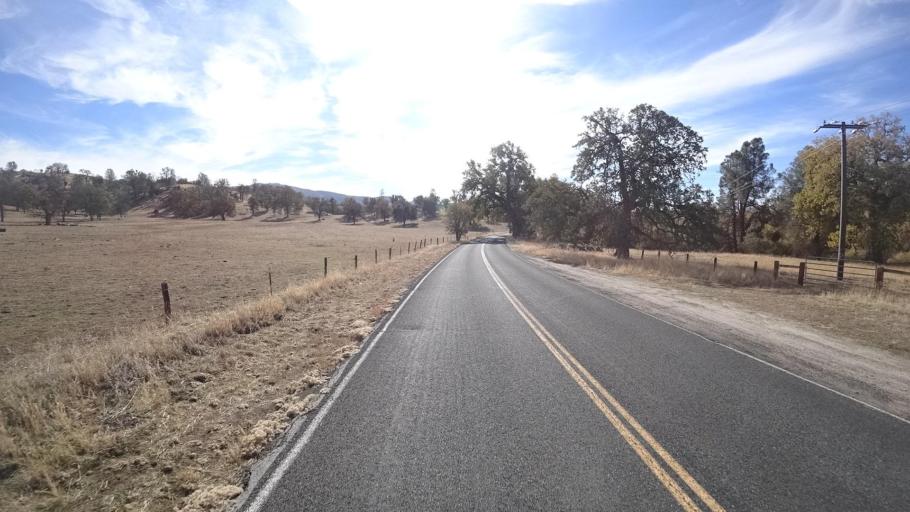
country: US
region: California
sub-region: Kern County
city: Alta Sierra
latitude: 35.6854
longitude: -118.7312
